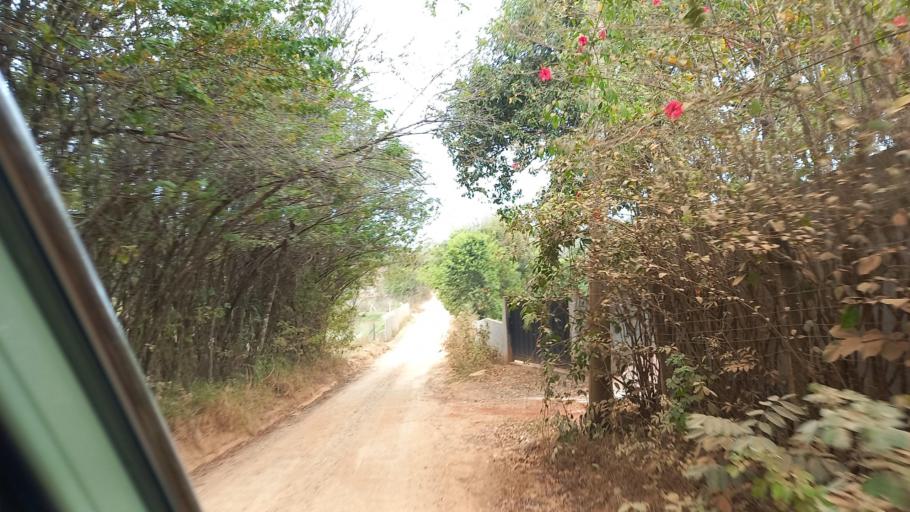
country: BR
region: Sao Paulo
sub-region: Moji-Guacu
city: Mogi-Gaucu
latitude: -22.2959
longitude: -46.8320
